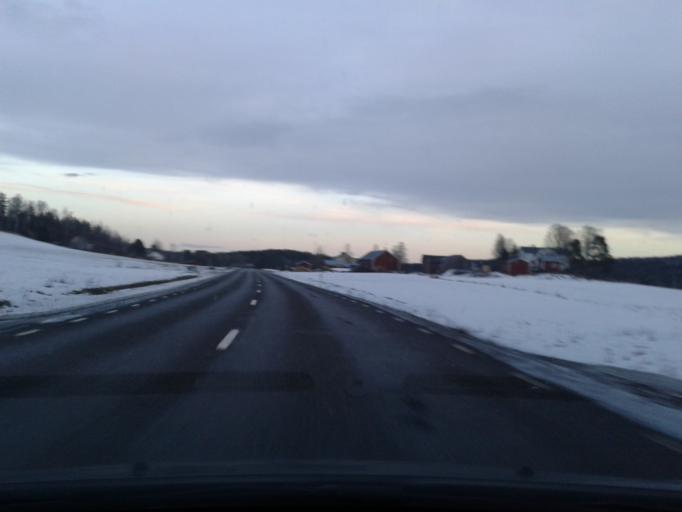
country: SE
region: Vaesternorrland
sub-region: Kramfors Kommun
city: Bollstabruk
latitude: 63.0777
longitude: 17.5448
